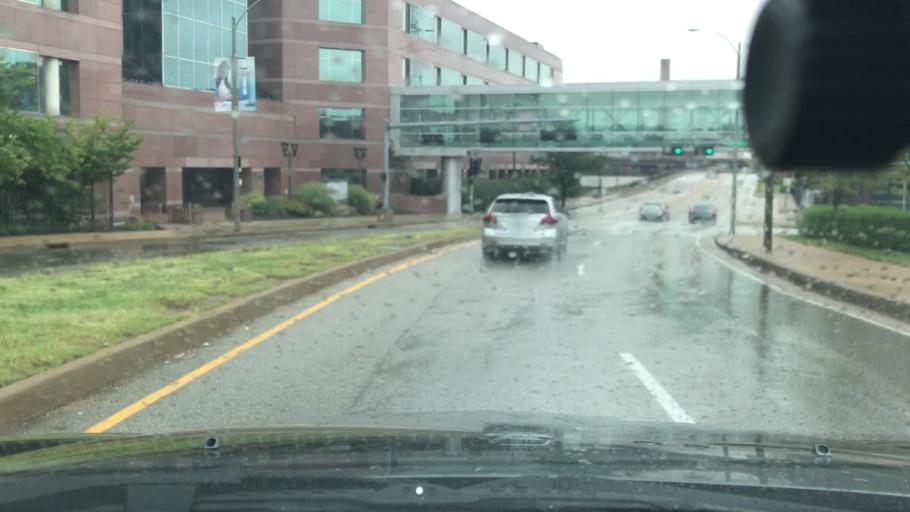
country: US
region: Missouri
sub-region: City of Saint Louis
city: St. Louis
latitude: 38.6218
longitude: -90.2086
